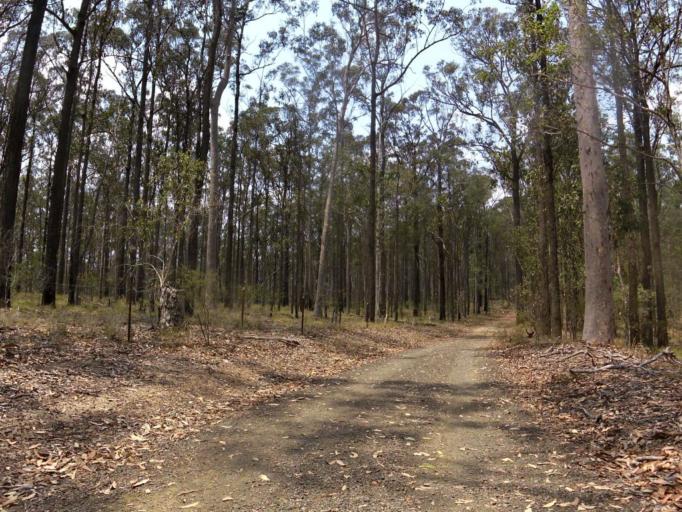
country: AU
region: Queensland
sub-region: Logan
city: Springwood
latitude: -27.6082
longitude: 153.1585
